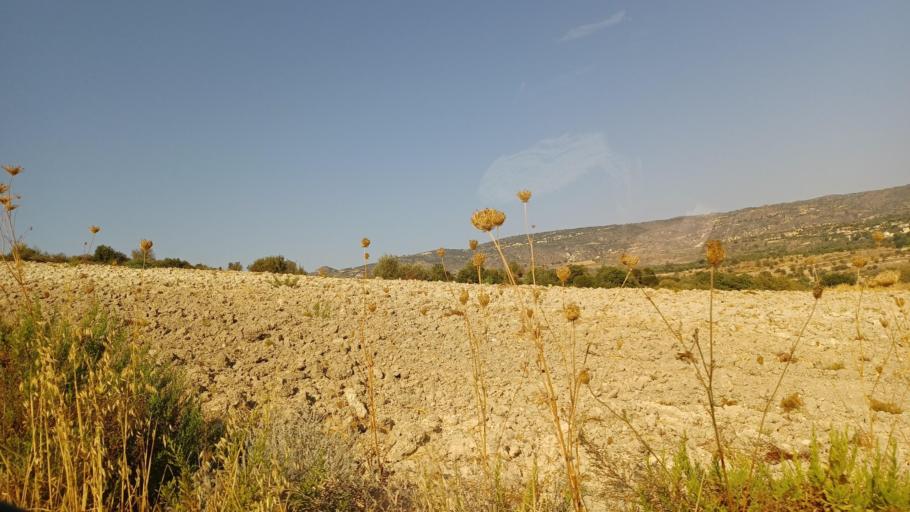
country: CY
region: Pafos
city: Tala
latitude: 34.9115
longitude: 32.4954
